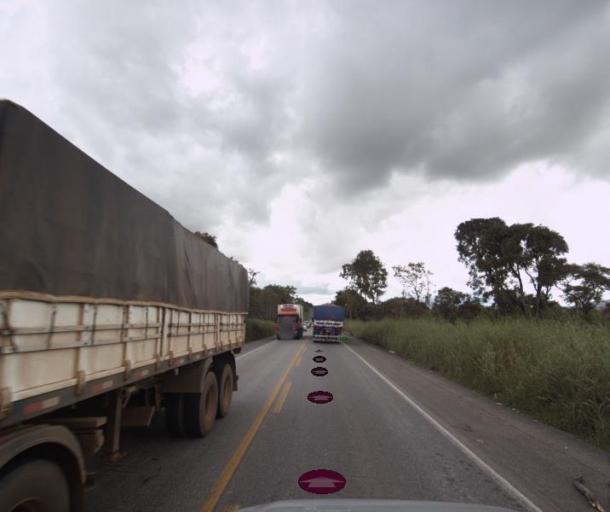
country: BR
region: Goias
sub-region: Uruacu
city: Uruacu
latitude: -14.2551
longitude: -49.1409
